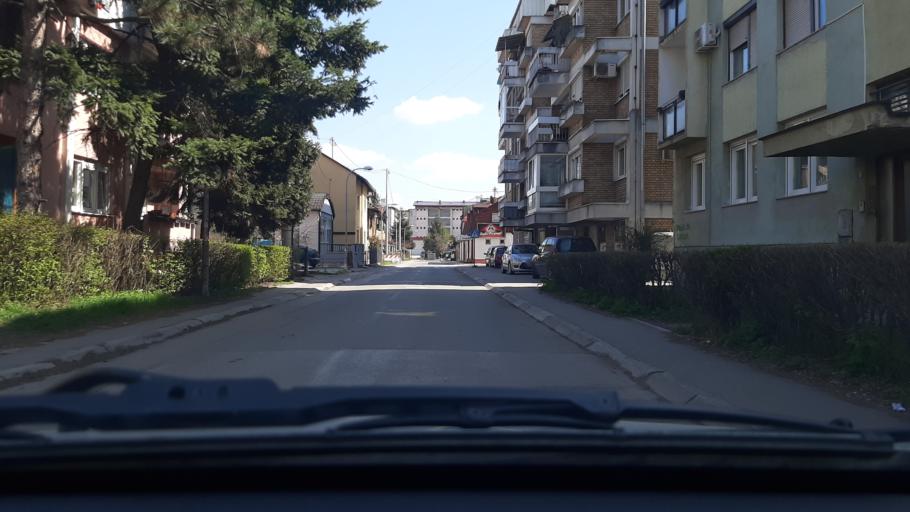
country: BA
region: Republika Srpska
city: Hiseti
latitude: 44.7676
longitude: 17.1829
